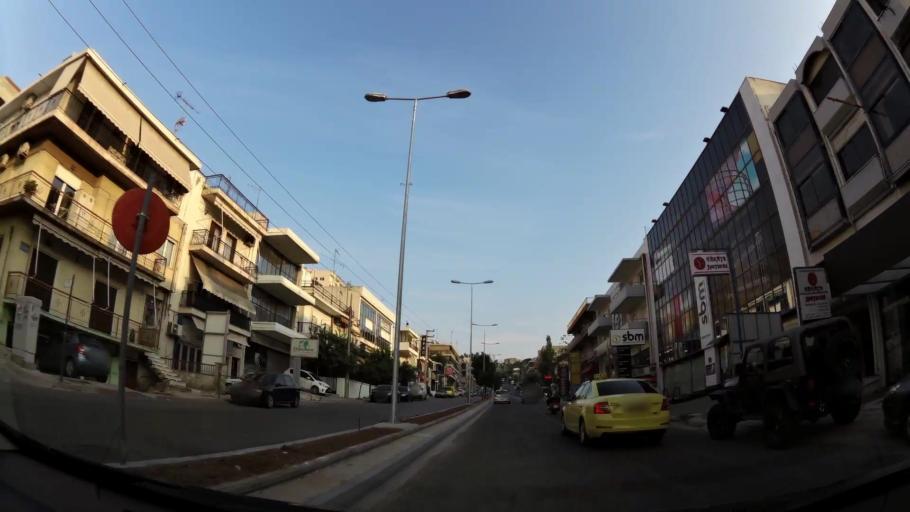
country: GR
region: Attica
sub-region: Nomarchia Athinas
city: Galatsi
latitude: 38.0100
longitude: 23.7578
